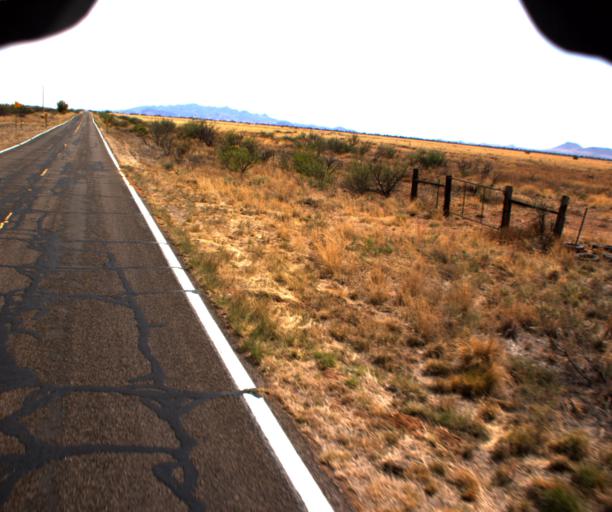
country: US
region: Arizona
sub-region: Cochise County
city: Willcox
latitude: 31.9149
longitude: -109.4915
